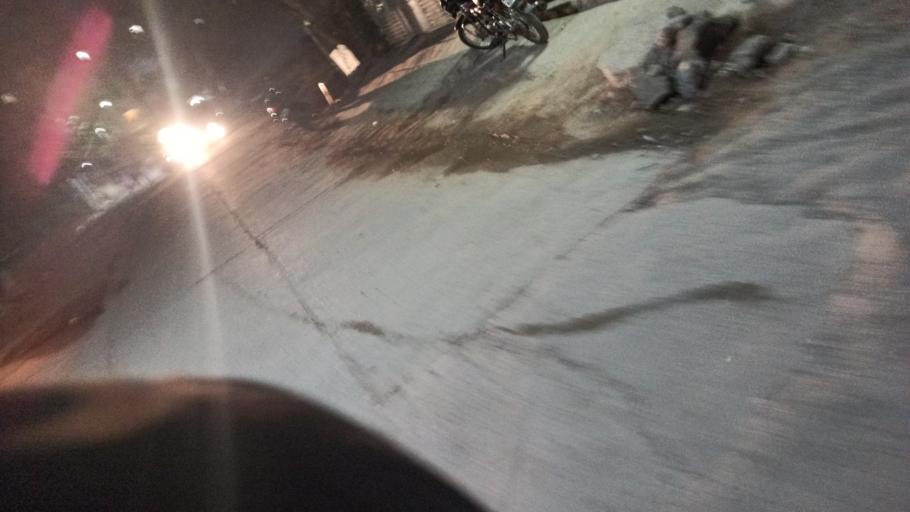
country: IN
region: Telangana
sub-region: Rangareddi
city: Kukatpalli
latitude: 17.5224
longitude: 78.3902
